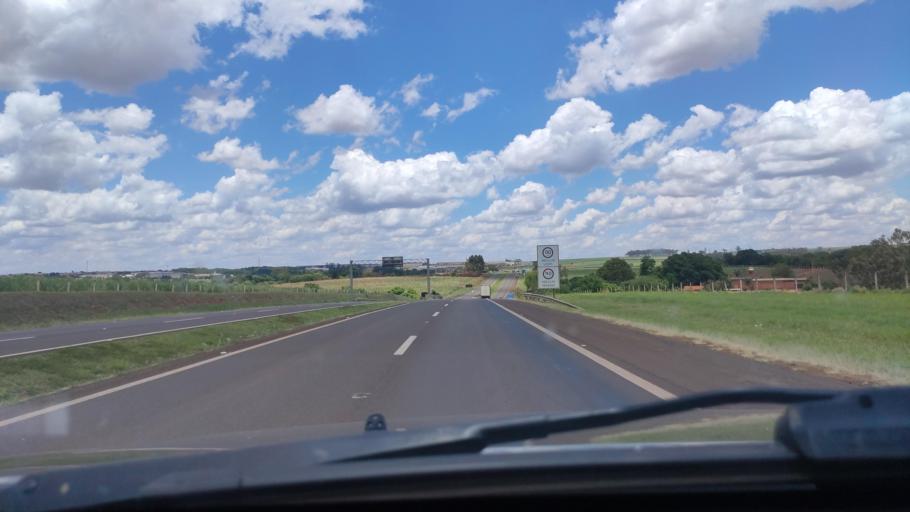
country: BR
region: Sao Paulo
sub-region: Pederneiras
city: Pederneiras
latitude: -22.3281
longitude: -48.7426
